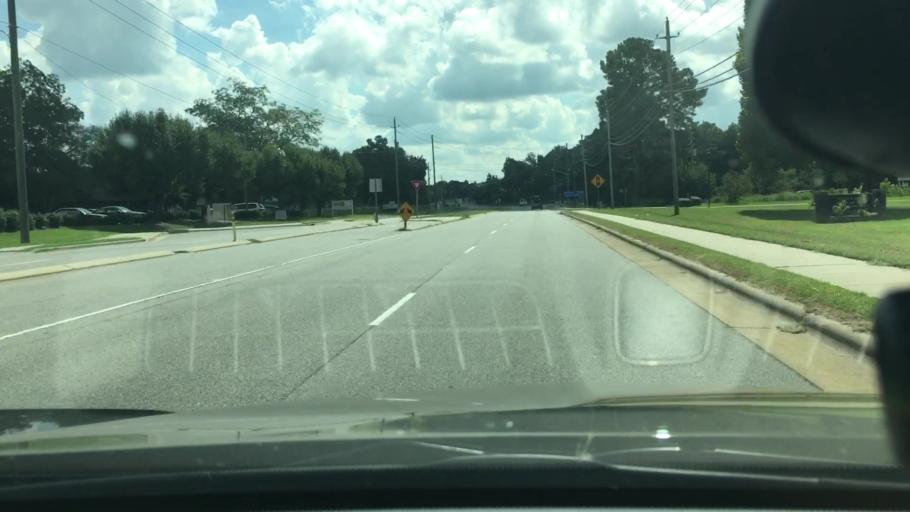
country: US
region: North Carolina
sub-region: Pitt County
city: Greenville
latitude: 35.6176
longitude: -77.4120
